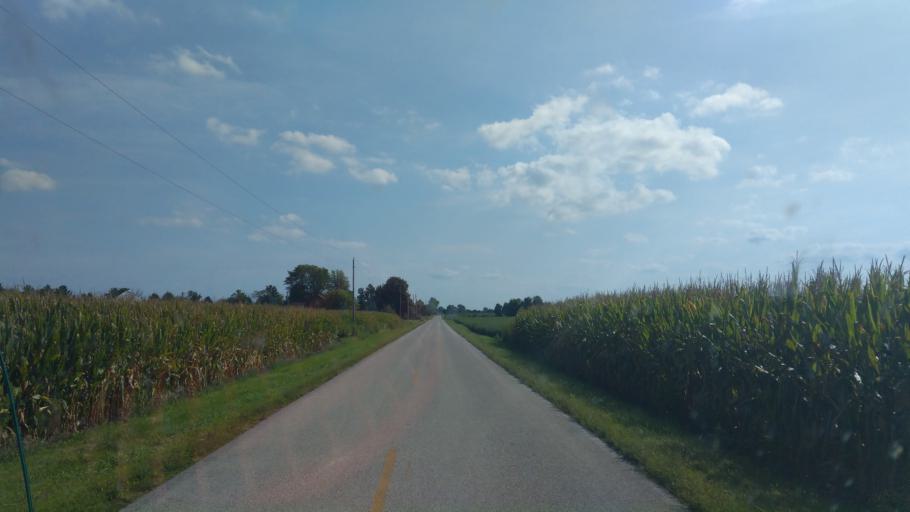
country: US
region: Ohio
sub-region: Hardin County
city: Forest
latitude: 40.6986
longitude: -83.5144
